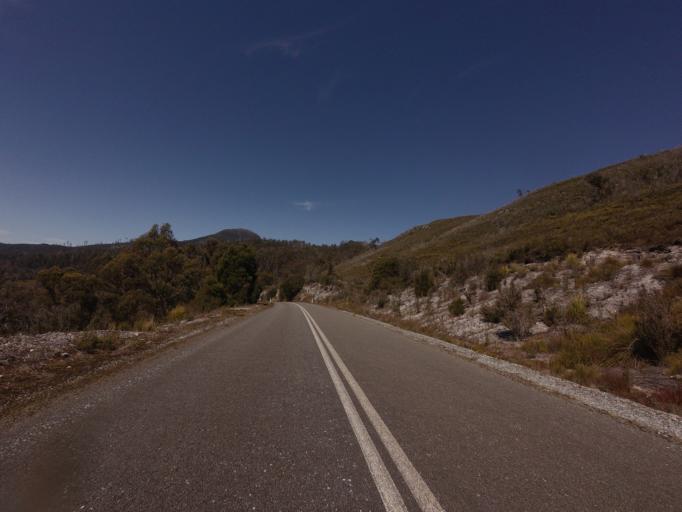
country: AU
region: Tasmania
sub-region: Huon Valley
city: Geeveston
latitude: -42.8463
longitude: 146.2419
